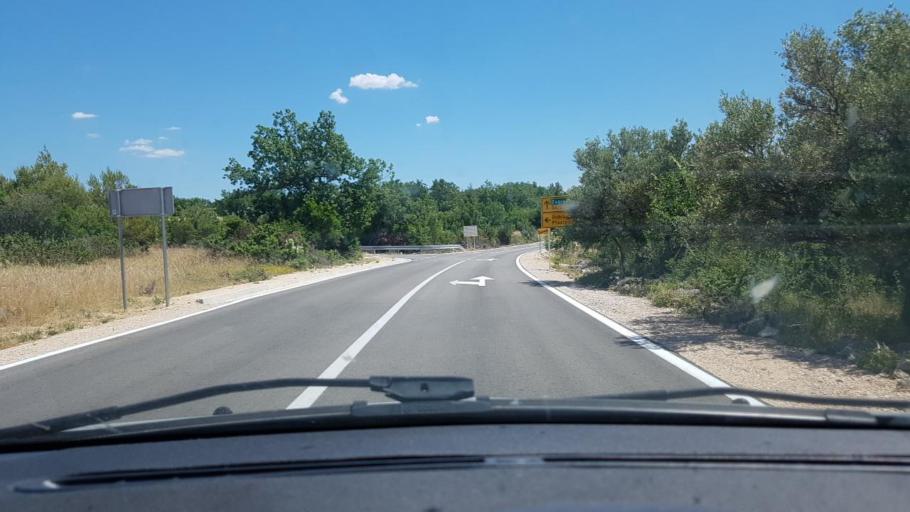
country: HR
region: Sibensko-Kniniska
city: Kistanje
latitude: 43.8838
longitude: 15.9137
